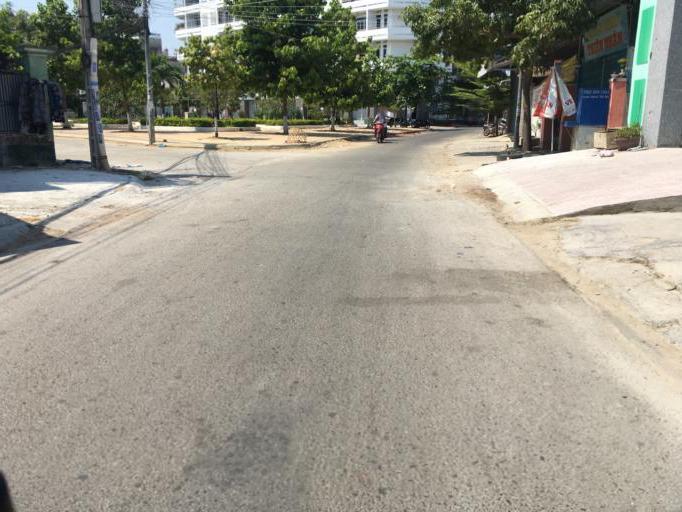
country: VN
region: Ninh Thuan
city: Phan Rang-Thap Cham
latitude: 11.5687
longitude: 108.9940
